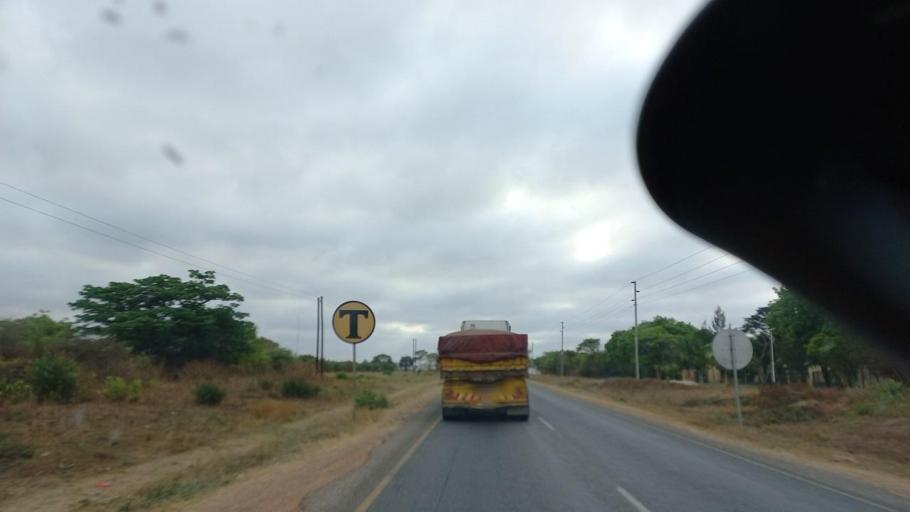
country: ZM
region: Lusaka
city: Chongwe
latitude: -15.3512
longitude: 28.5581
